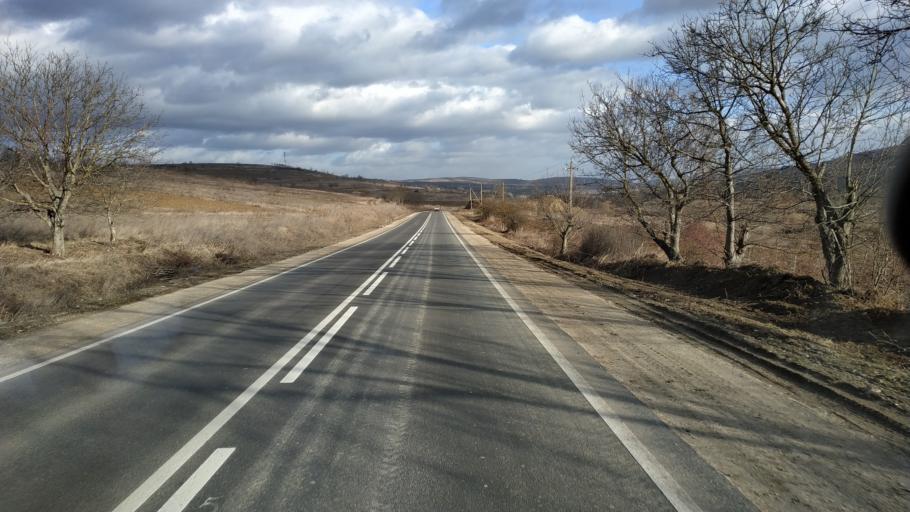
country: MD
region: Calarasi
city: Calarasi
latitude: 47.2953
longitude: 28.1642
